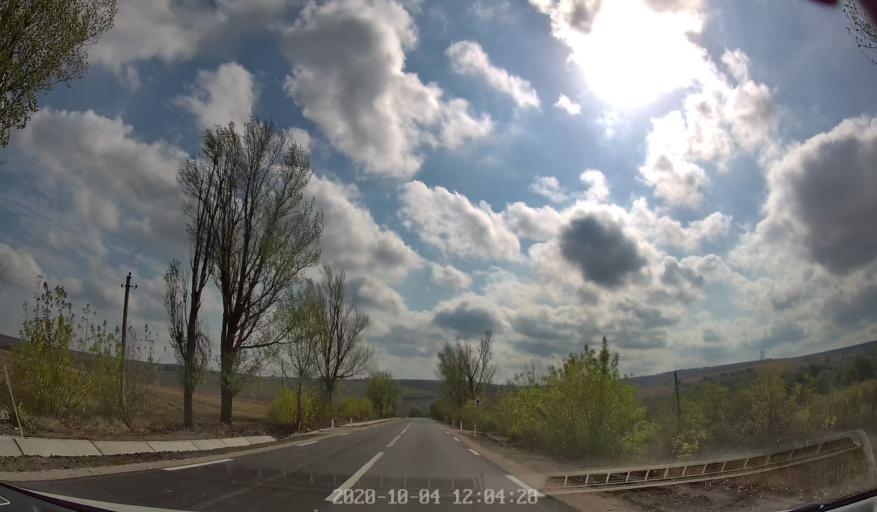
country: MD
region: Rezina
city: Saharna
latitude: 47.6035
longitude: 28.9433
